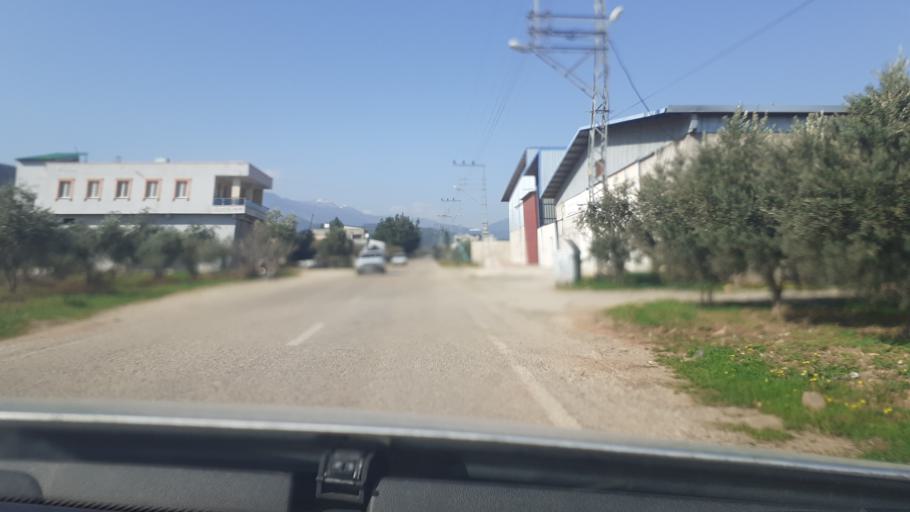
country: TR
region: Hatay
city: Aktepe
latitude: 36.7127
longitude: 36.4859
